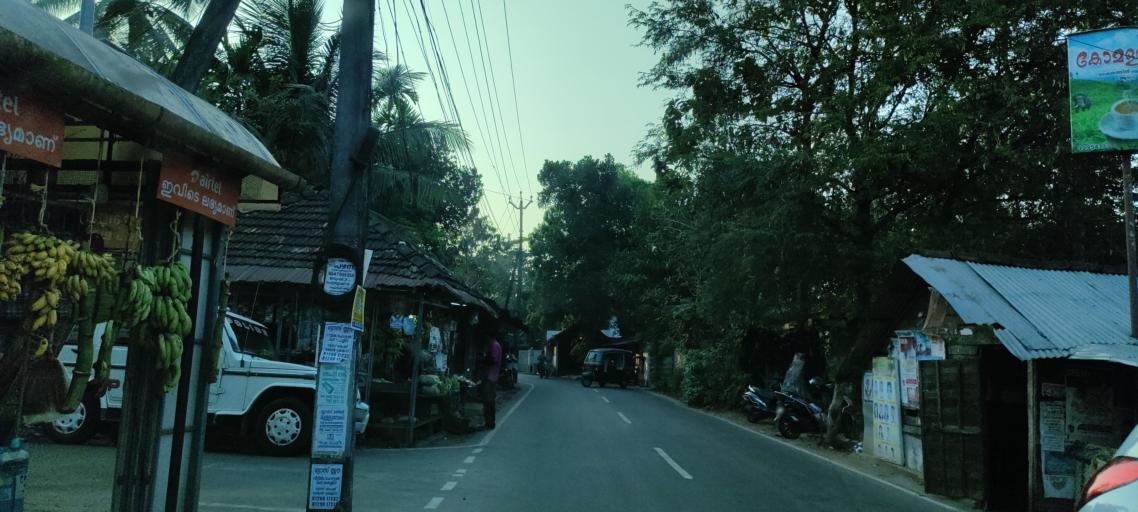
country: IN
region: Kerala
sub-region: Alappuzha
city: Alleppey
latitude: 9.5402
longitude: 76.3354
